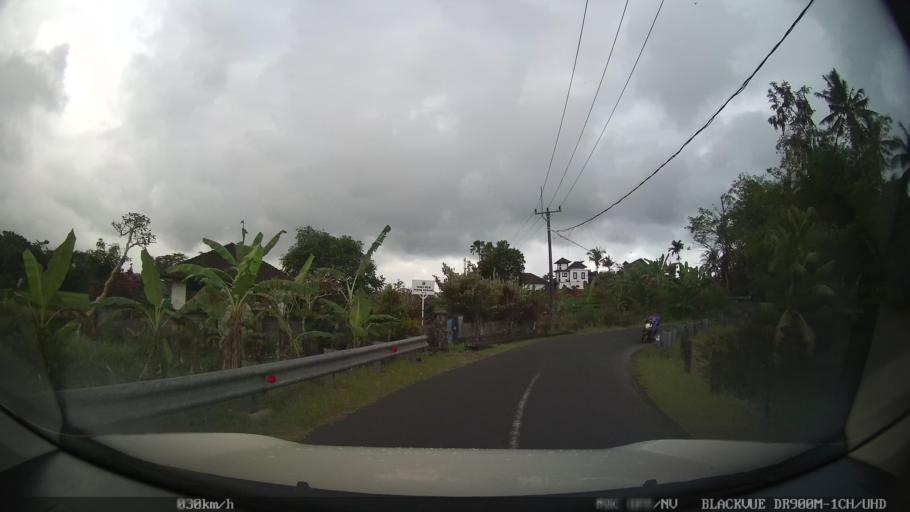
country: ID
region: Bali
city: Banjar Cemenggon
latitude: -8.5327
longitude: 115.1926
